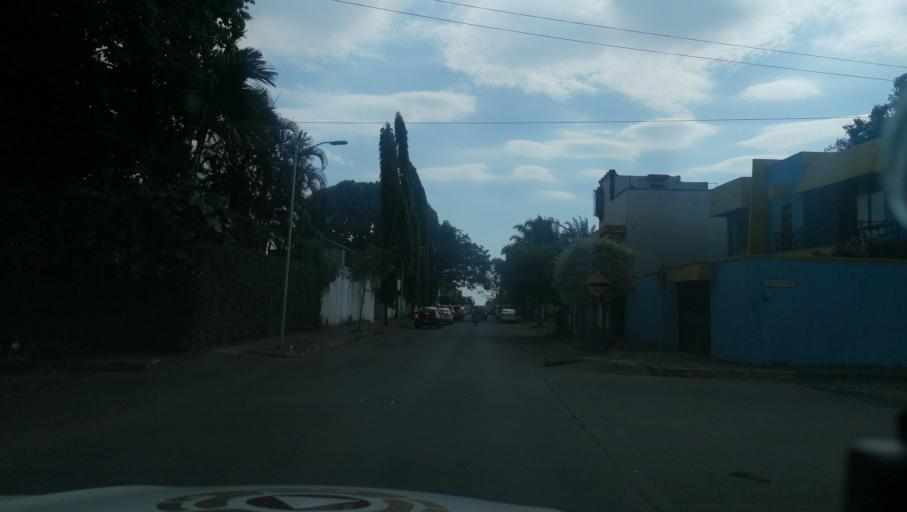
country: MX
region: Chiapas
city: Tapachula
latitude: 14.9144
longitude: -92.2542
